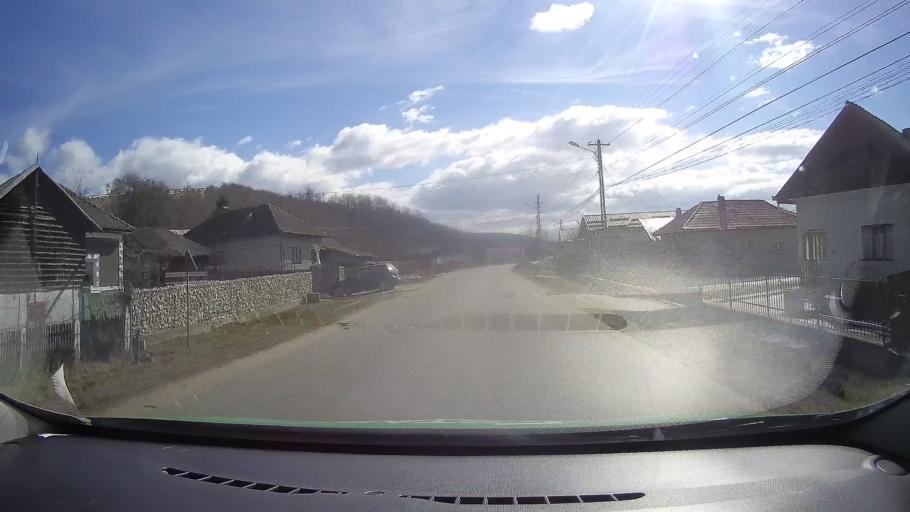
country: RO
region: Dambovita
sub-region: Comuna Vulcana-Pandele
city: Gura Vulcanei
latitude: 45.0351
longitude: 25.3924
